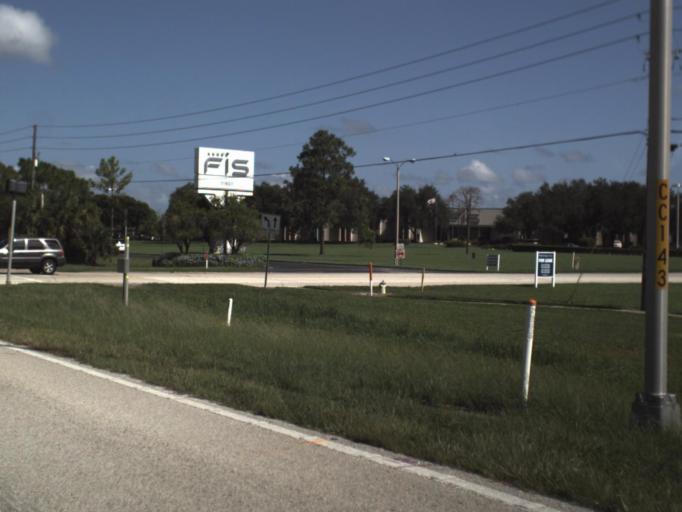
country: US
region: Florida
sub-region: Pinellas County
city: Feather Sound
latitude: 27.8750
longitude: -82.6535
